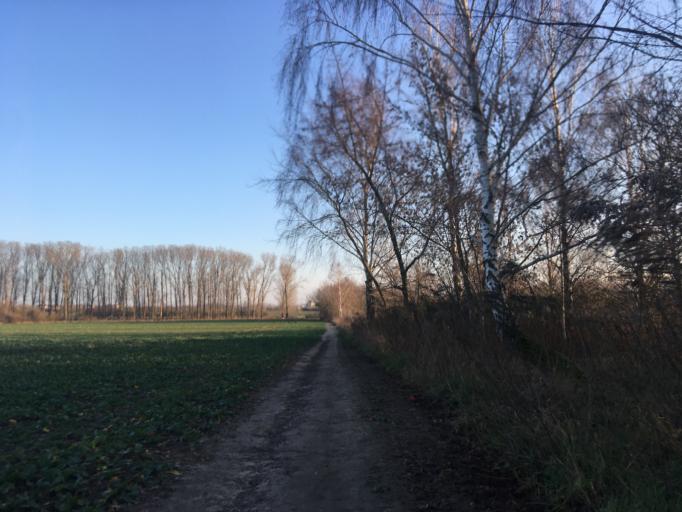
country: DE
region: Berlin
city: Karow
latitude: 52.6041
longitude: 13.4911
